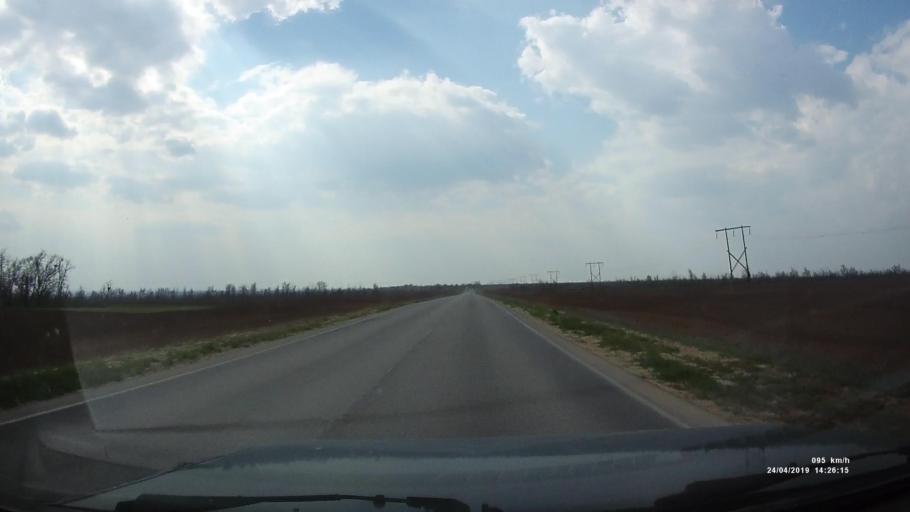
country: RU
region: Kalmykiya
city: Arshan'
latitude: 46.3332
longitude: 44.0659
